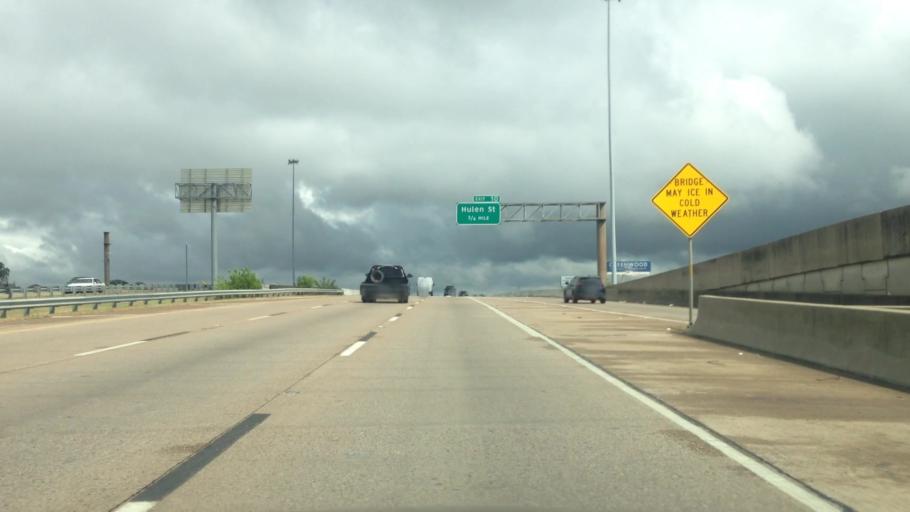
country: US
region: Texas
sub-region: Tarrant County
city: Westworth
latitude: 32.7339
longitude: -97.4061
